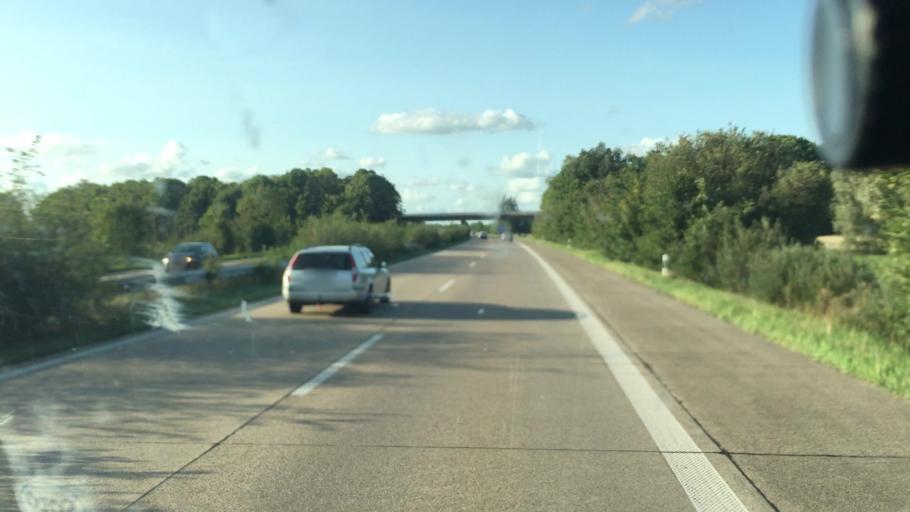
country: DE
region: Lower Saxony
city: Sande
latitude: 53.4724
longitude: 8.0158
